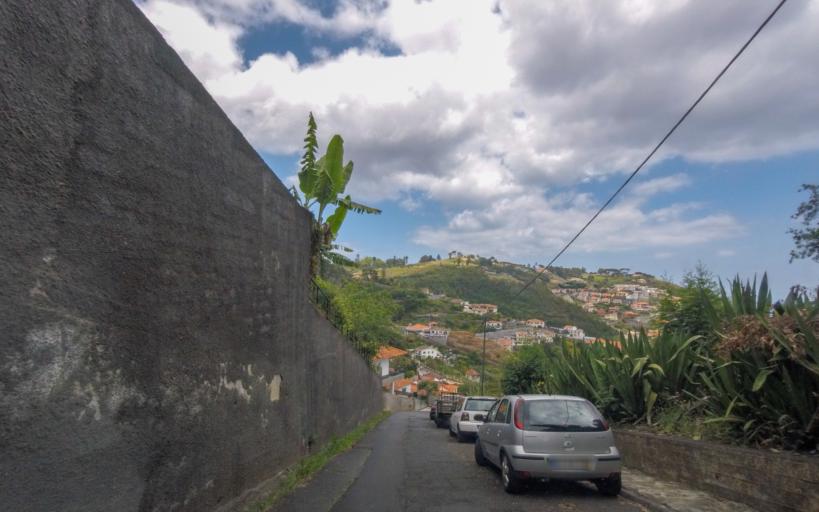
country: PT
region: Madeira
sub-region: Funchal
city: Nossa Senhora do Monte
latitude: 32.6624
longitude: -16.8788
